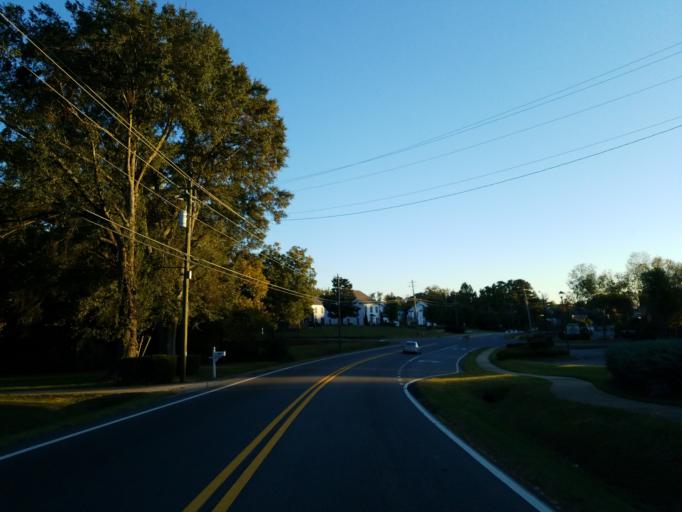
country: US
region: Georgia
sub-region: Forsyth County
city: Cumming
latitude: 34.2138
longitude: -84.1352
